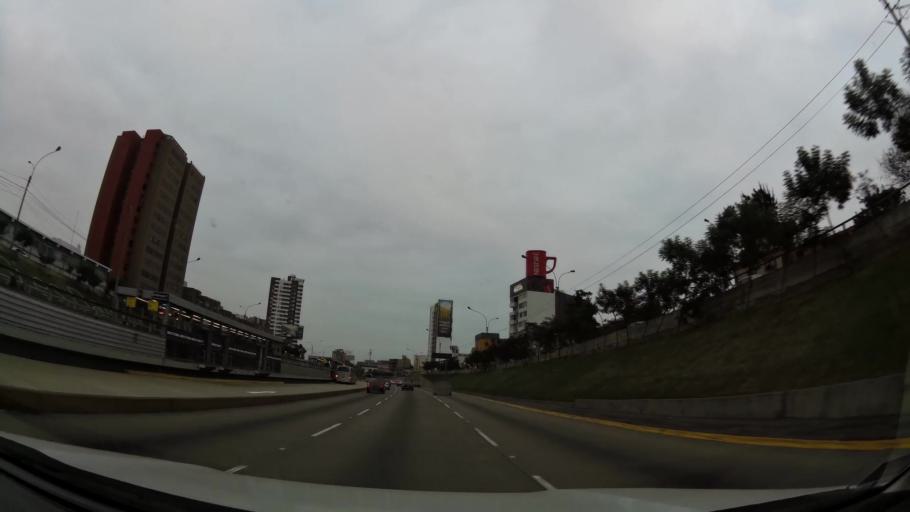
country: PE
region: Lima
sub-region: Lima
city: San Isidro
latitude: -12.1033
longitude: -77.0275
